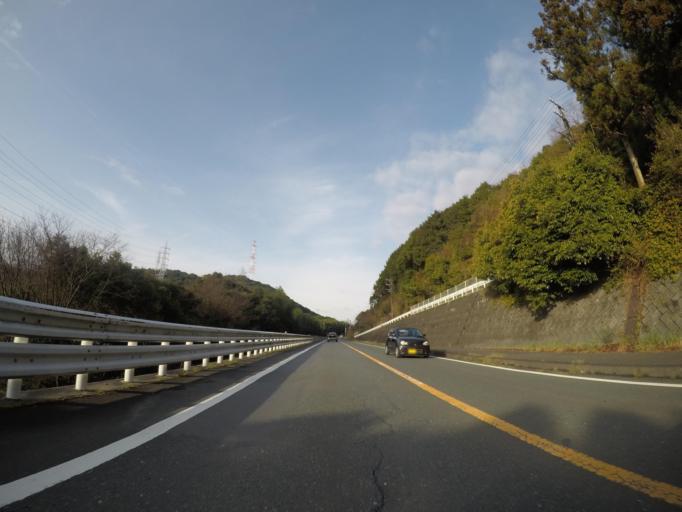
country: JP
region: Shizuoka
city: Hamakita
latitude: 34.8166
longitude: 137.7019
